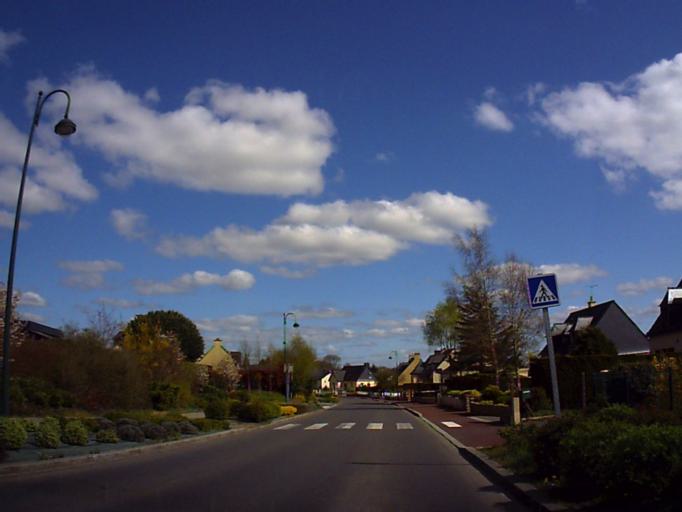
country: FR
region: Brittany
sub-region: Departement d'Ille-et-Vilaine
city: Saint-Meen-le-Grand
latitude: 48.1783
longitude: -2.1815
